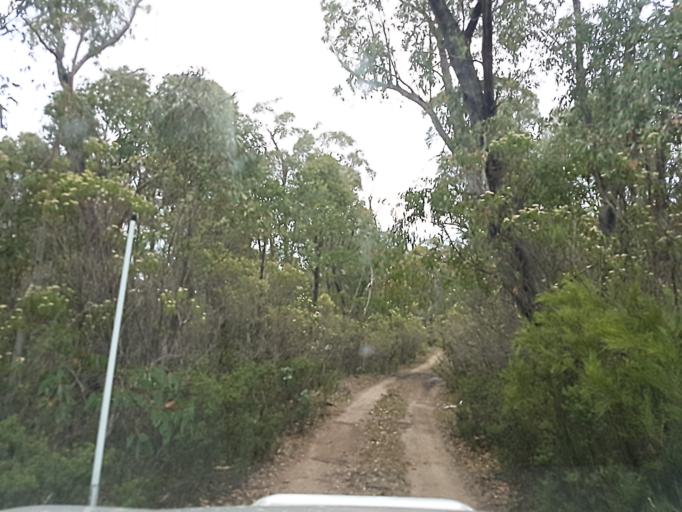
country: AU
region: New South Wales
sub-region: Snowy River
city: Jindabyne
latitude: -36.8641
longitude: 148.2657
